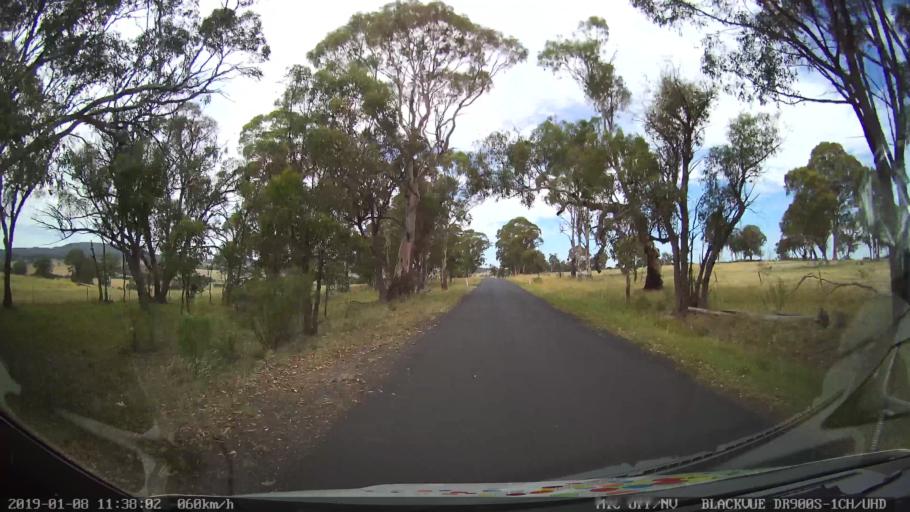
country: AU
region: New South Wales
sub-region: Guyra
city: Guyra
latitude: -30.3568
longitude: 151.5552
